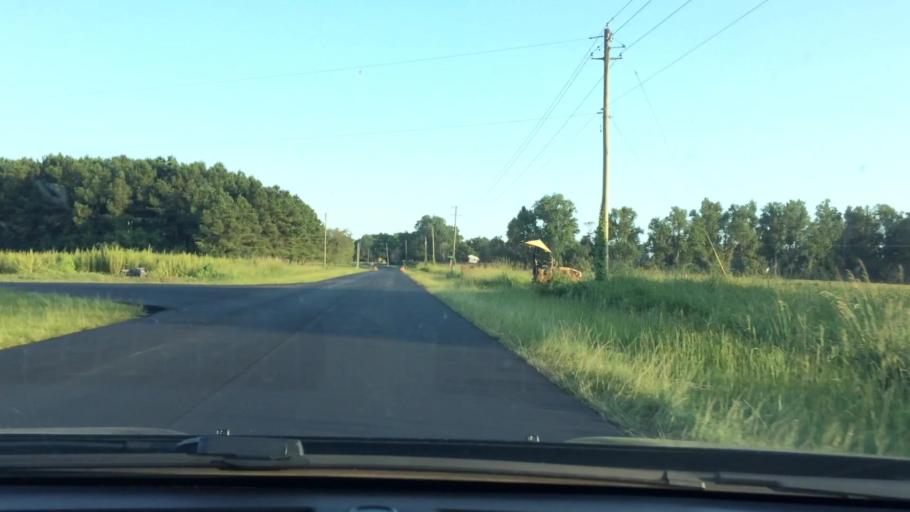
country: US
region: North Carolina
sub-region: Pitt County
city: Ayden
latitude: 35.4320
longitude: -77.4503
